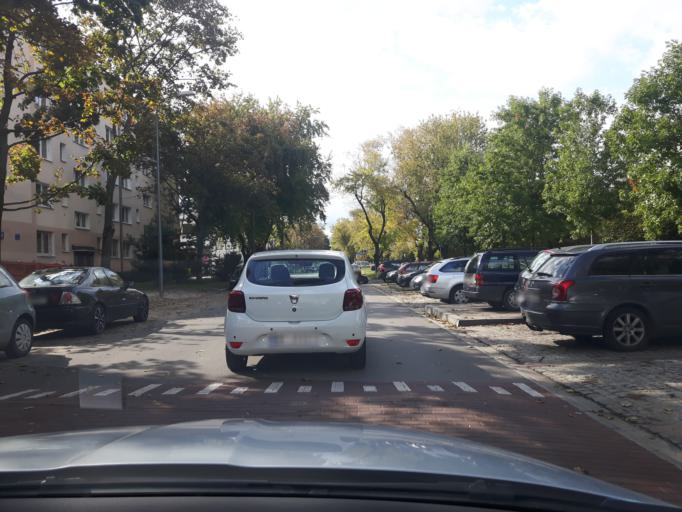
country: PL
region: Masovian Voivodeship
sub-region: Warszawa
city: Praga Poludnie
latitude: 52.2383
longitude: 21.0917
